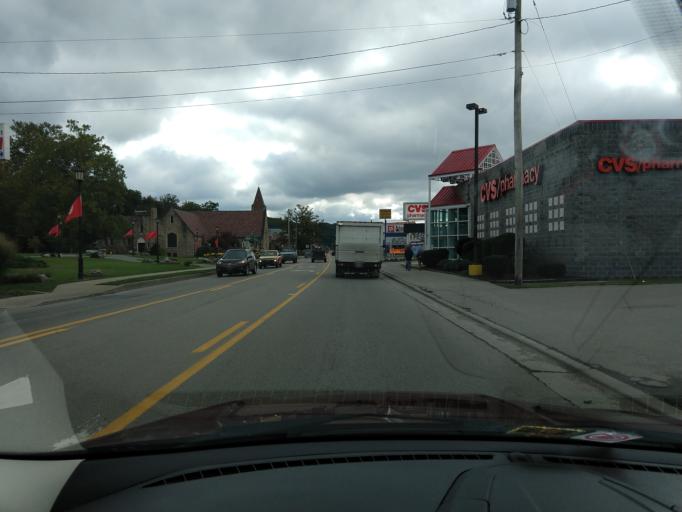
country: US
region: West Virginia
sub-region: Randolph County
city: Elkins
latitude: 38.9282
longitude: -79.8489
